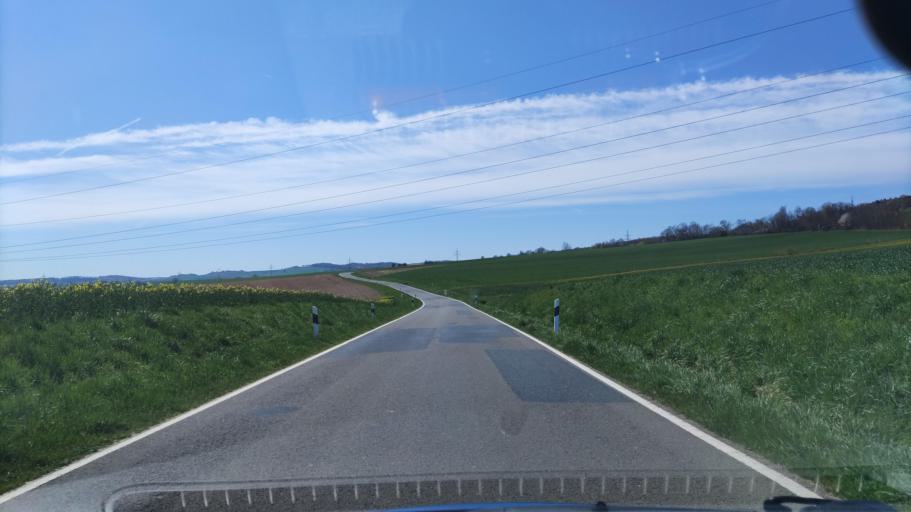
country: DE
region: Lower Saxony
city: Freden
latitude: 51.8841
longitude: 9.8540
